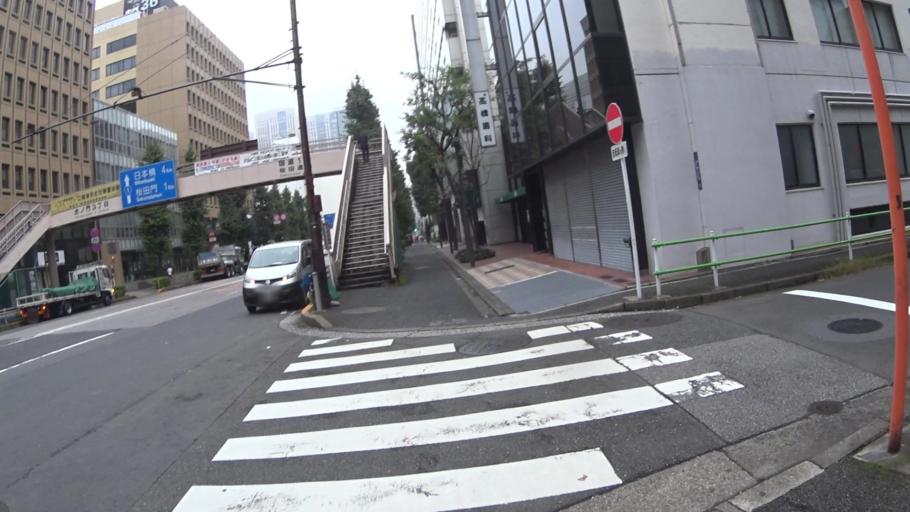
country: JP
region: Tokyo
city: Tokyo
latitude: 35.6653
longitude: 139.7470
